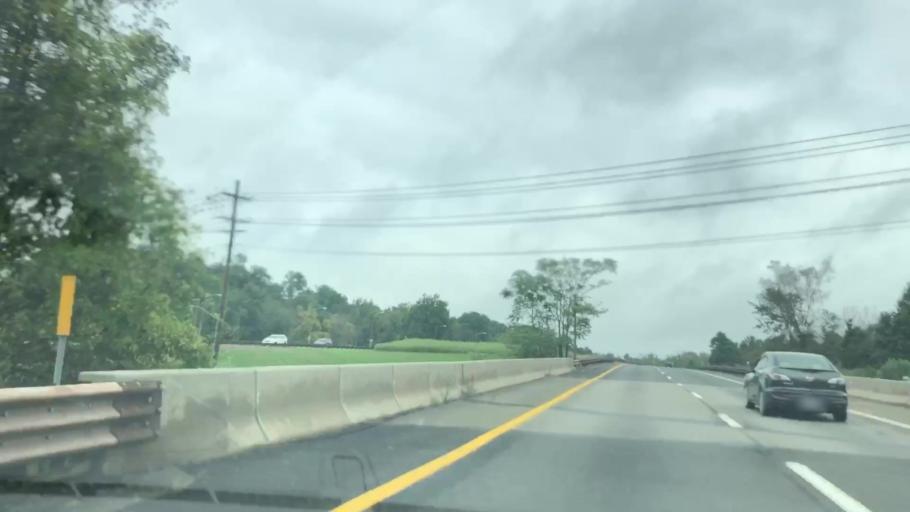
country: US
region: New Jersey
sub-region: Bergen County
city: Park Ridge
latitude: 41.0551
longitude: -74.0653
